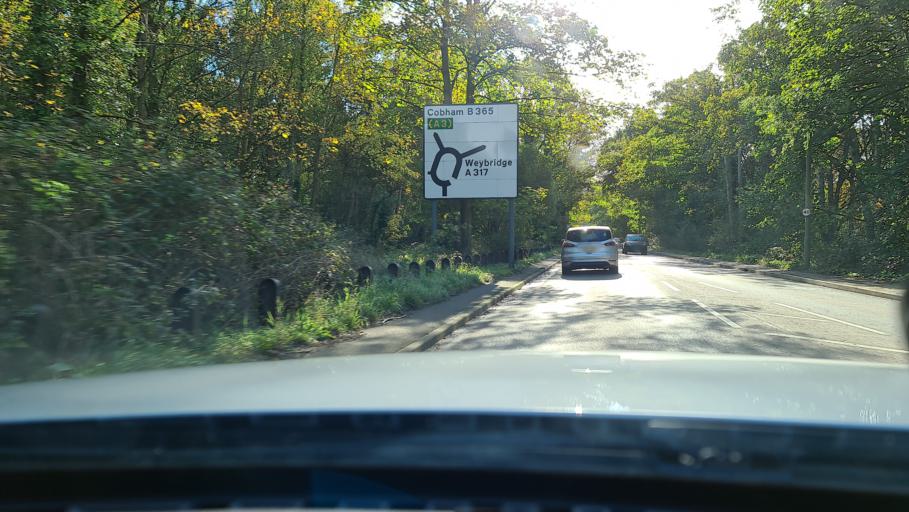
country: GB
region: England
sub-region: Surrey
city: Walton-on-Thames
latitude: 51.3675
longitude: -0.4292
